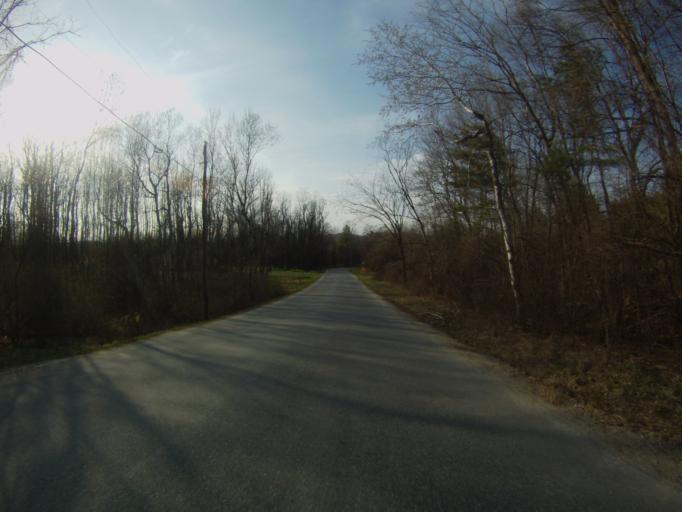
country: US
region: Vermont
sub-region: Addison County
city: Middlebury (village)
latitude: 44.0092
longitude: -73.2175
